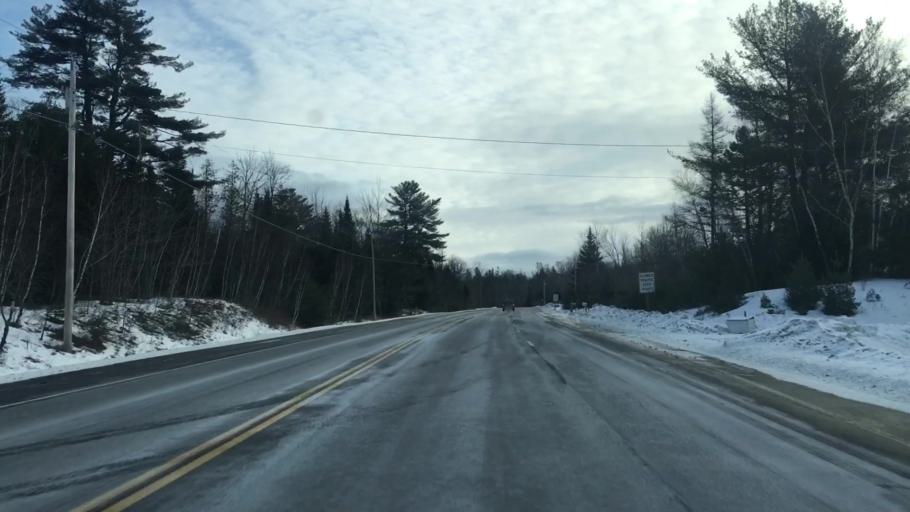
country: US
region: Maine
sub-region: Washington County
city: Machias
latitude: 44.9503
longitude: -67.6751
